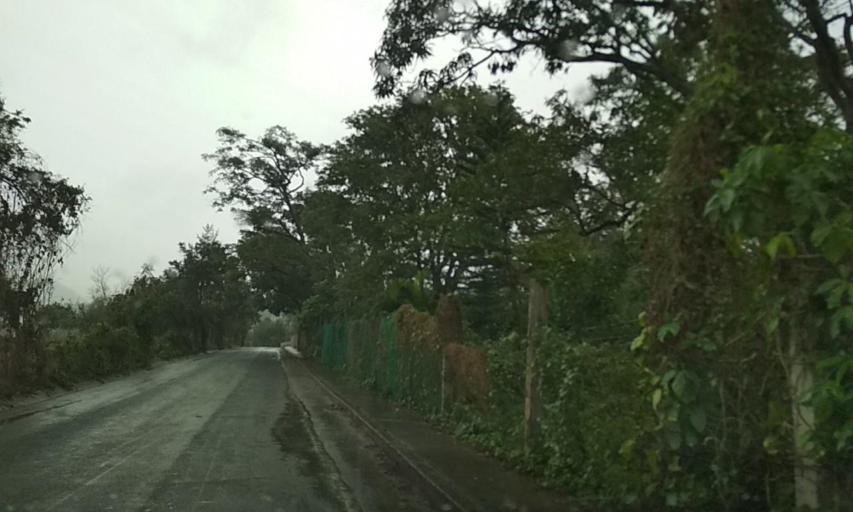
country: MX
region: Veracruz
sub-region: Papantla
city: El Chote
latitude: 20.4004
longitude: -97.3441
